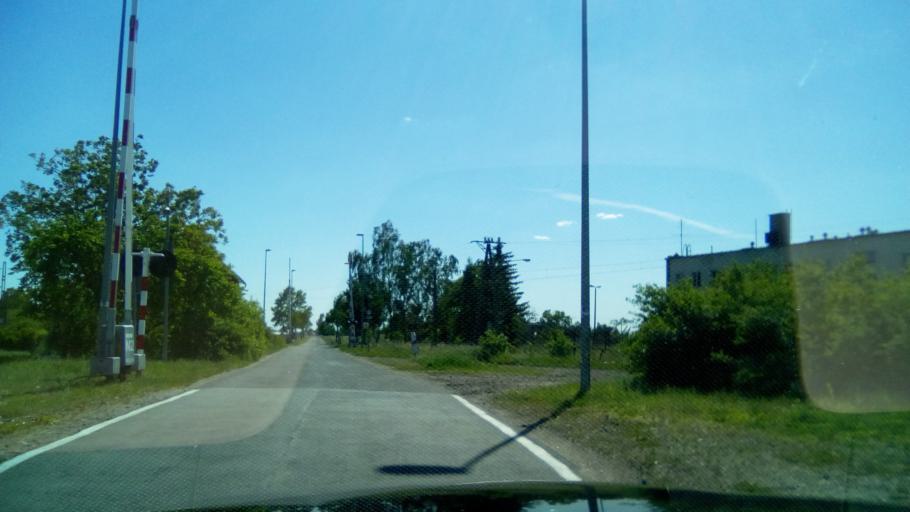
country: PL
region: Greater Poland Voivodeship
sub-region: Powiat gnieznienski
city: Gniezno
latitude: 52.4812
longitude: 17.5700
